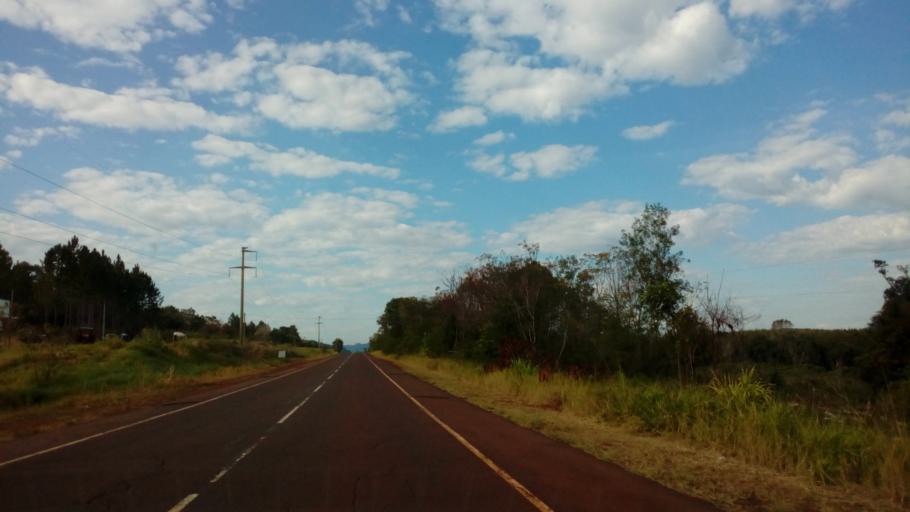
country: AR
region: Misiones
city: Ruiz de Montoya
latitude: -27.0646
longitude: -54.9948
